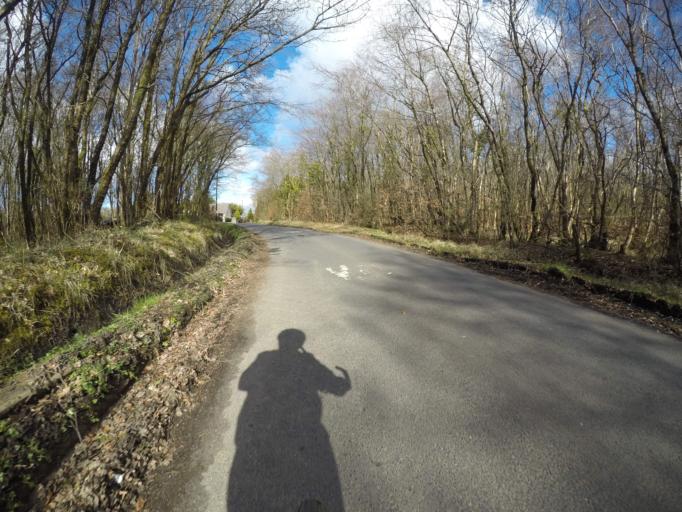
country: GB
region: Scotland
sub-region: North Ayrshire
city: Irvine
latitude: 55.6722
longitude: -4.6563
